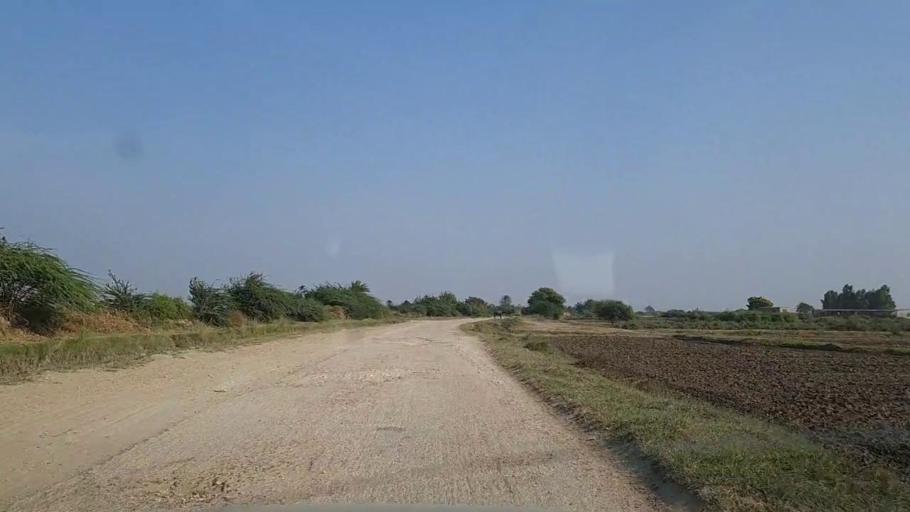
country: PK
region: Sindh
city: Mirpur Sakro
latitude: 24.5959
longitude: 67.5974
